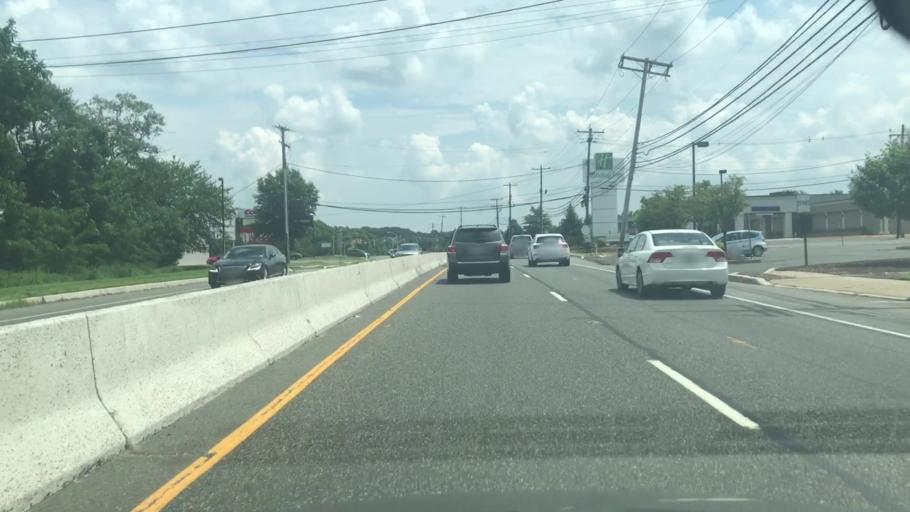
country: US
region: New Jersey
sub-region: Monmouth County
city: Union Beach
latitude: 40.4174
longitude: -74.1731
